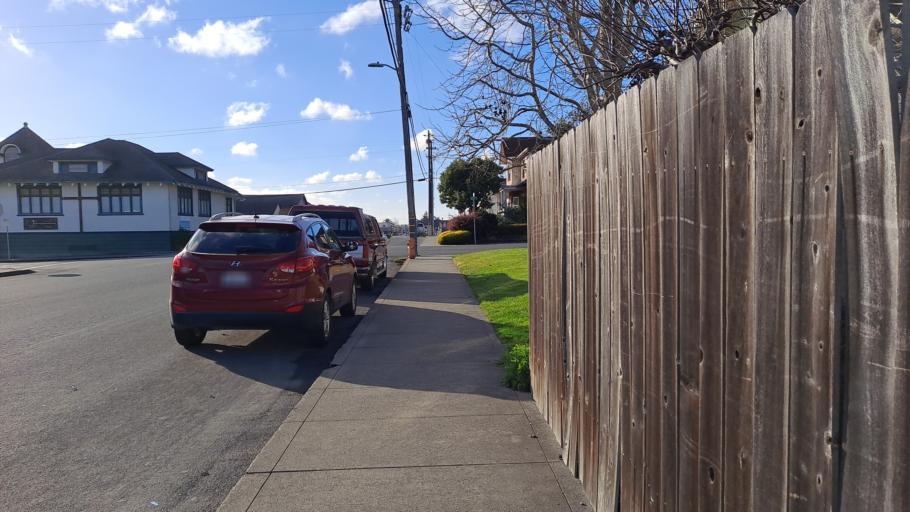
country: US
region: California
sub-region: Humboldt County
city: Fortuna
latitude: 40.5989
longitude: -124.1530
